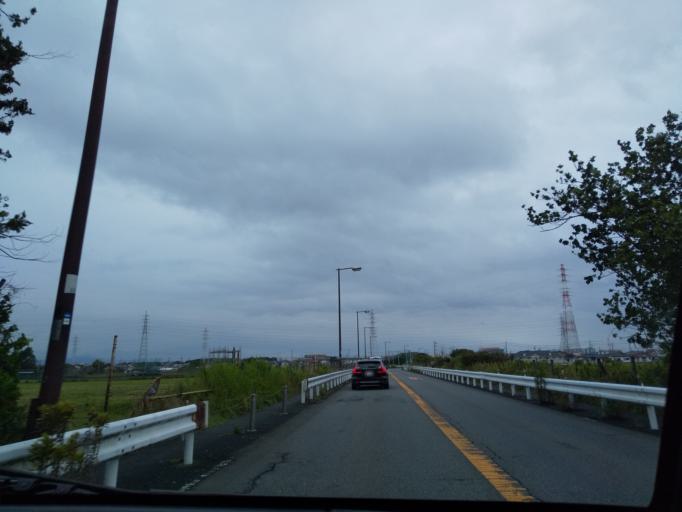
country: JP
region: Kanagawa
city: Fujisawa
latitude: 35.3999
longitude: 139.5027
